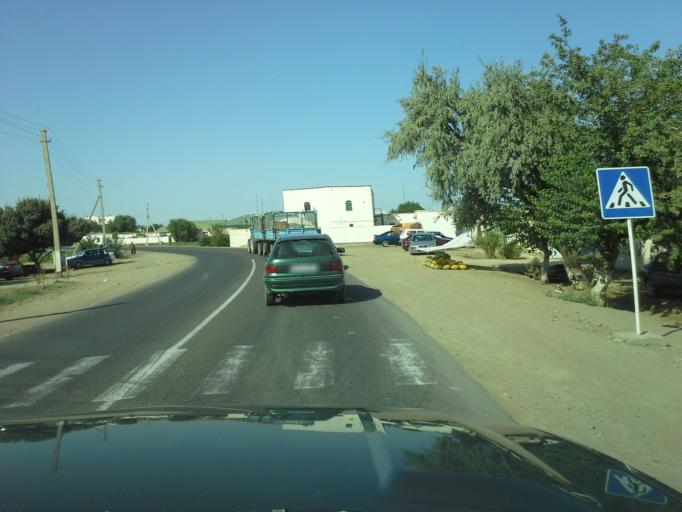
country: TM
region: Dasoguz
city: Dasoguz
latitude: 41.8233
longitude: 59.9539
